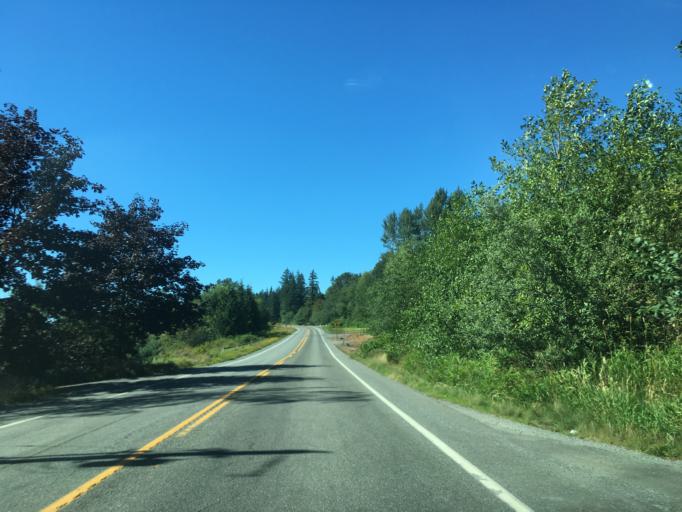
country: US
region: Washington
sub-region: Skagit County
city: Big Lake
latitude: 48.3615
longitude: -122.2052
